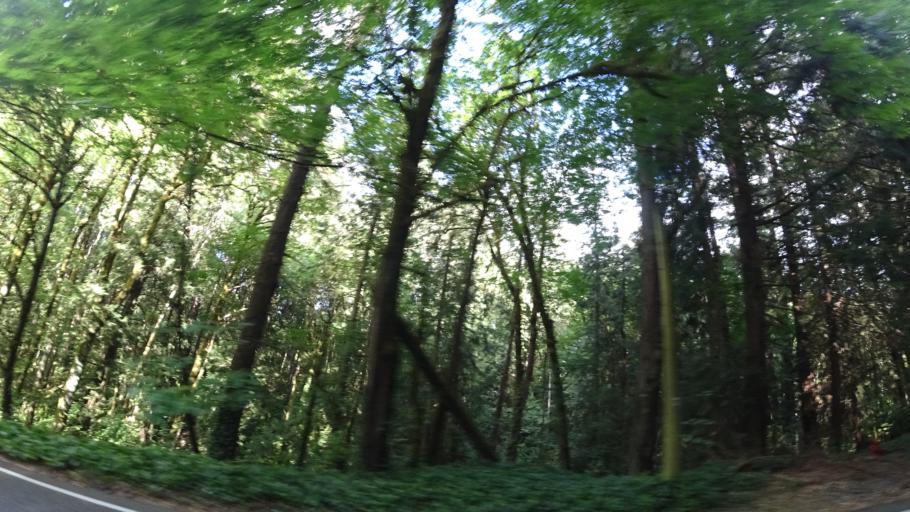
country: US
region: Oregon
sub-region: Washington County
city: Garden Home-Whitford
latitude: 45.4699
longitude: -122.7231
